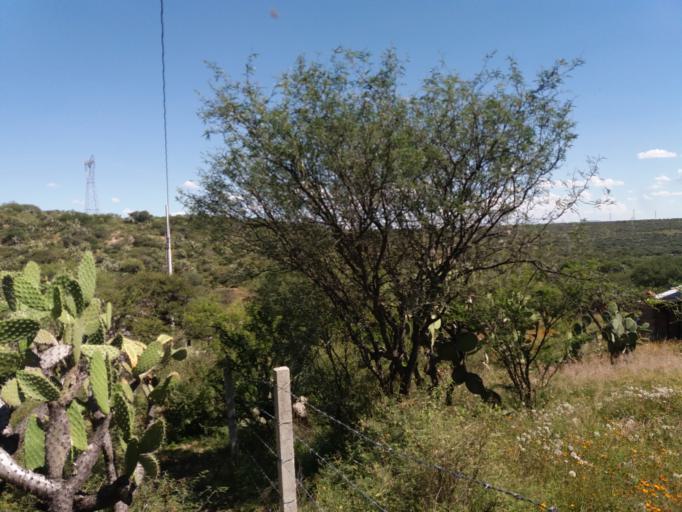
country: MX
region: Aguascalientes
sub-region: Aguascalientes
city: Villa Licenciado Jesus Teran (Calvillito)
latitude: 21.7824
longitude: -102.2254
